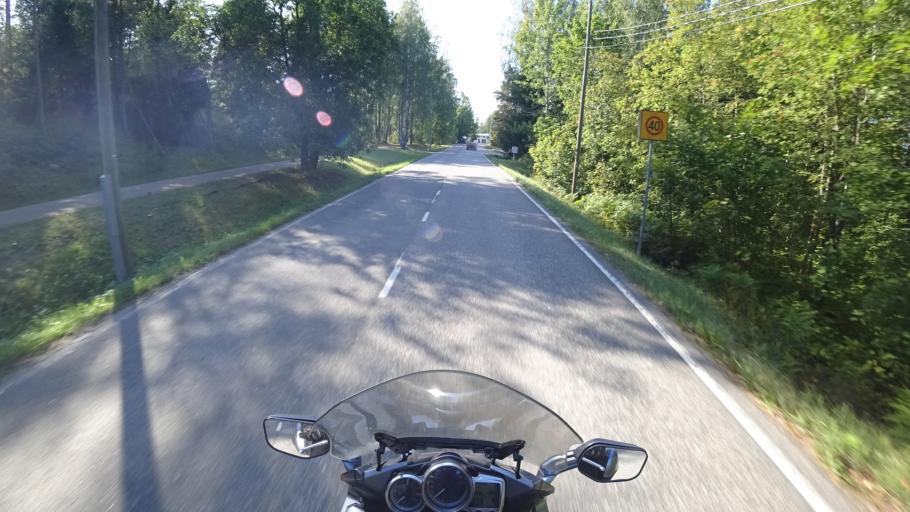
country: FI
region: Uusimaa
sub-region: Helsinki
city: Sammatti
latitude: 60.3179
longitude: 23.8269
